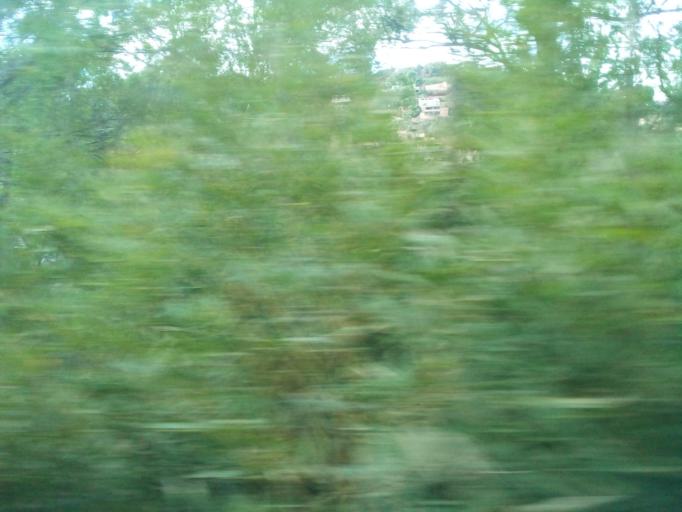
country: BR
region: Minas Gerais
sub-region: Belo Horizonte
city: Belo Horizonte
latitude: -19.8728
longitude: -43.8522
